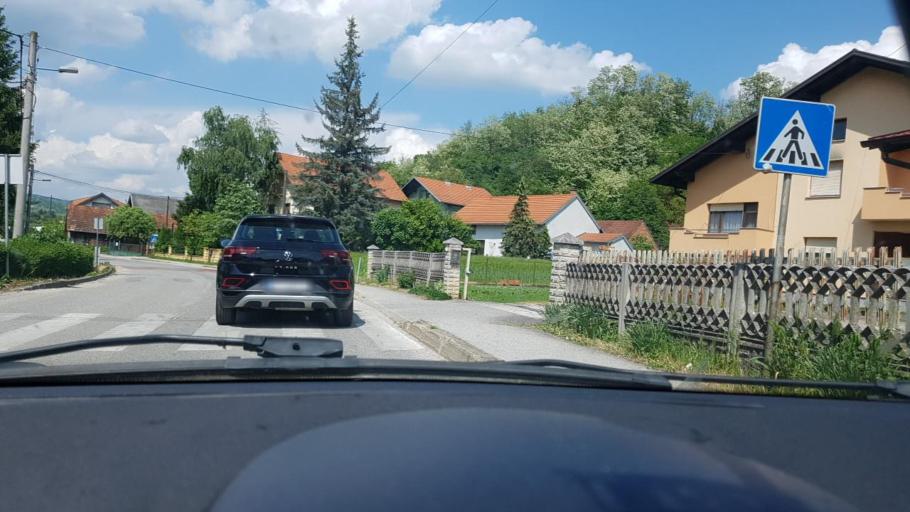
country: HR
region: Grad Zagreb
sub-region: Sesvete
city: Sesvete
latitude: 45.9067
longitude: 16.1639
